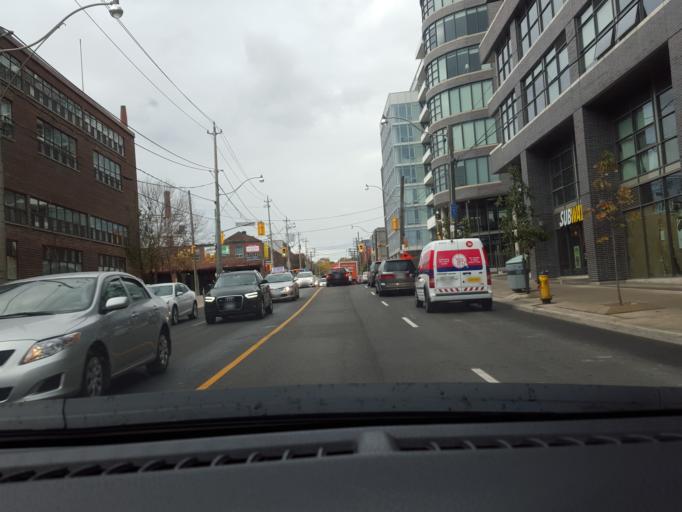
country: CA
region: Ontario
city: Toronto
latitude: 43.6642
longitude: -79.3413
